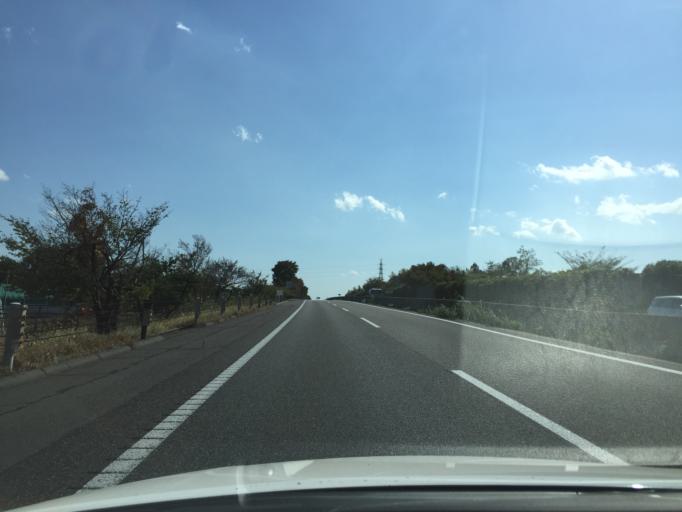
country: JP
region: Fukushima
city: Sukagawa
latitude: 37.3074
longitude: 140.3464
